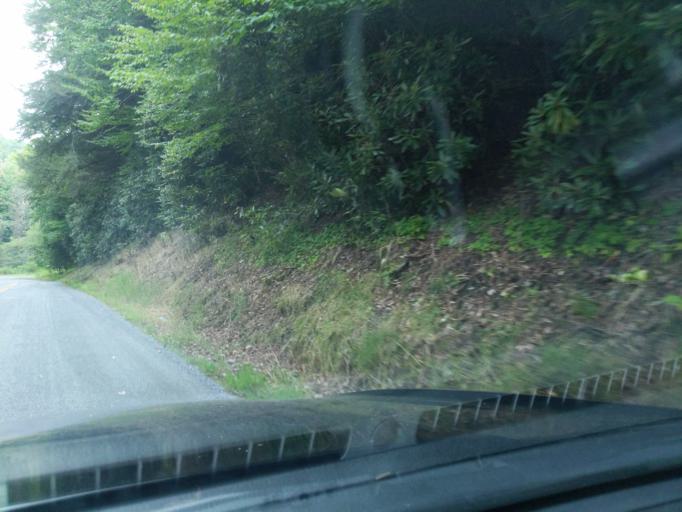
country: US
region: Pennsylvania
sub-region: Cambria County
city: Portage
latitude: 40.3334
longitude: -78.5800
